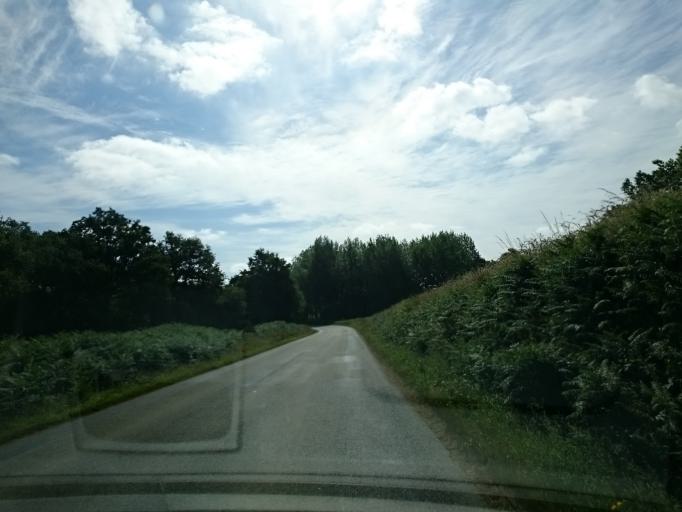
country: FR
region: Brittany
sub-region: Departement d'Ille-et-Vilaine
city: Chanteloup
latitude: 47.9429
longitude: -1.6245
